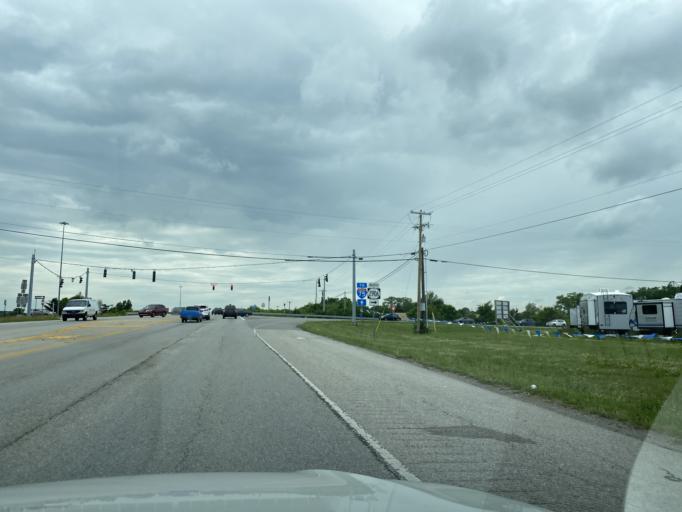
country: US
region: Kentucky
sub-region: Scott County
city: Georgetown
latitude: 38.2167
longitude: -84.5322
